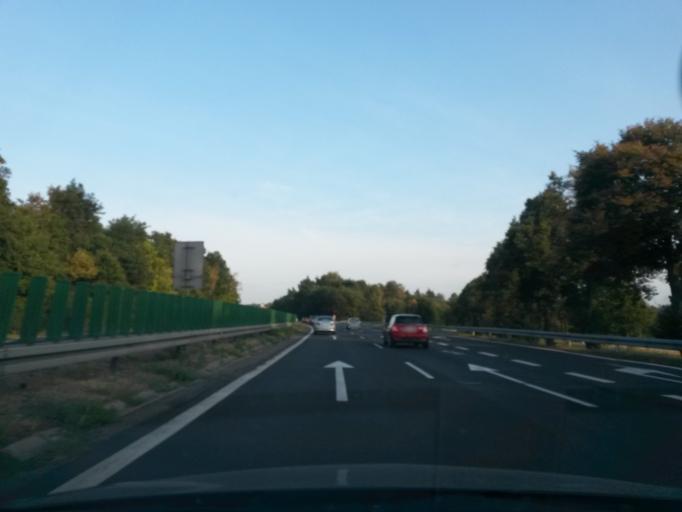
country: PL
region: Masovian Voivodeship
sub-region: Powiat nowodworski
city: Zakroczym
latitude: 52.4552
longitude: 20.5809
